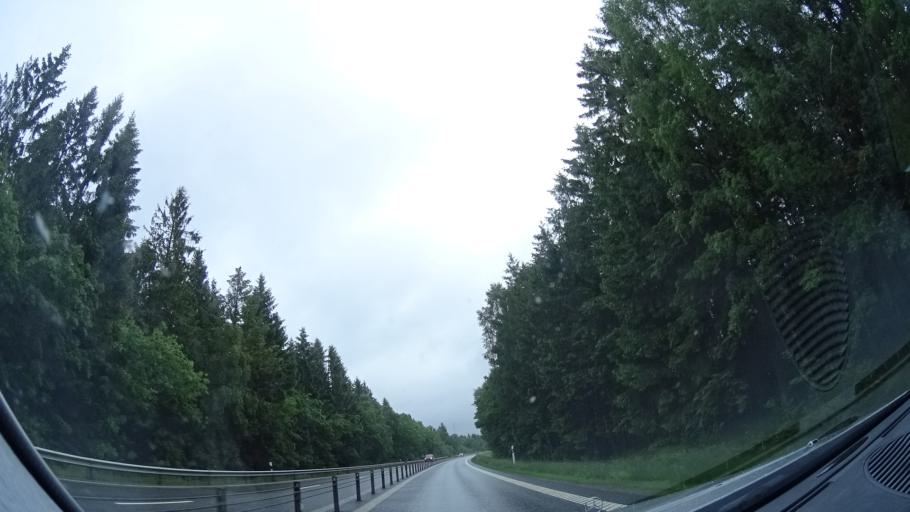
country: SE
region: Skane
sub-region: Hoors Kommun
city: Hoeoer
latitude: 55.9151
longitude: 13.5281
